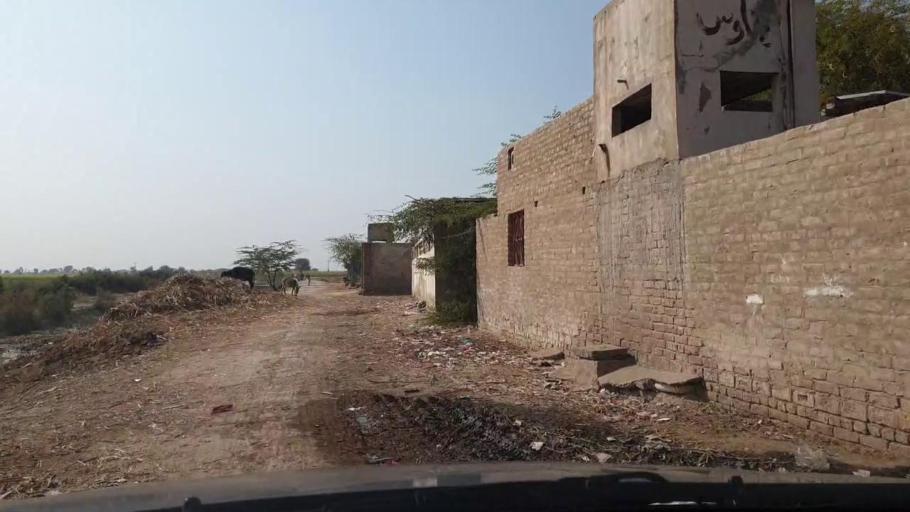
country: PK
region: Sindh
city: Sanghar
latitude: 26.0169
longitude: 68.9139
